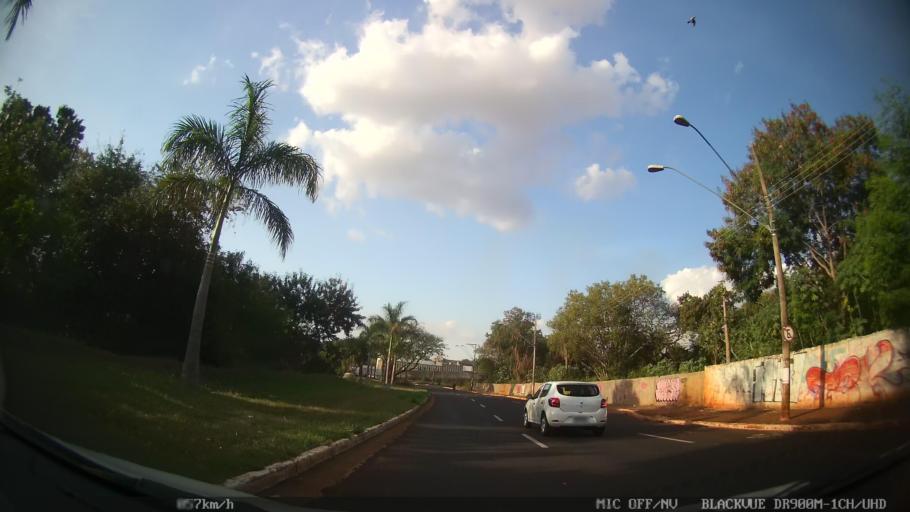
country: BR
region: Sao Paulo
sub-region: Ribeirao Preto
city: Ribeirao Preto
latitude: -21.1593
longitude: -47.8121
